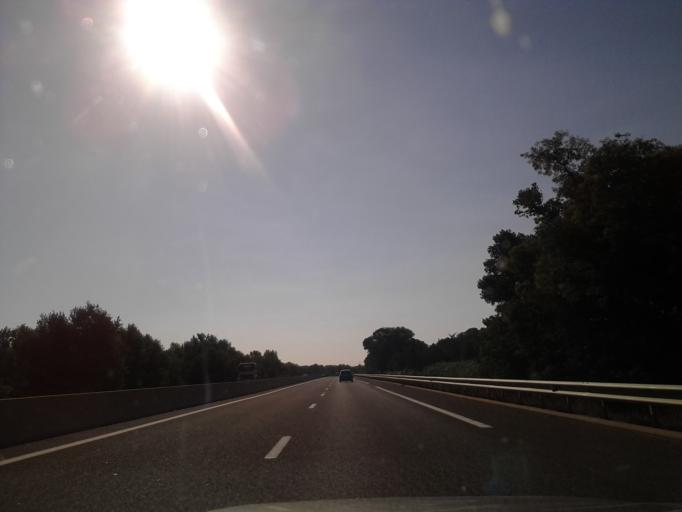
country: FR
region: Languedoc-Roussillon
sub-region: Departement des Pyrenees-Orientales
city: Corneilla-la-Riviere
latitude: 42.6904
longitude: 2.7201
